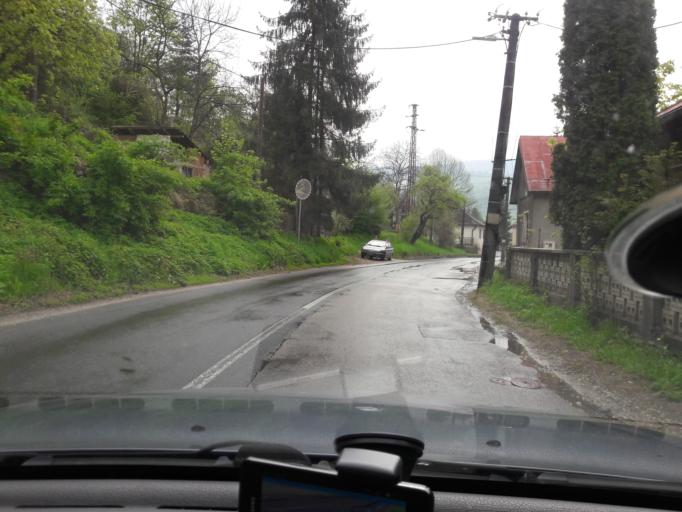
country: SK
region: Banskobystricky
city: Tisovec
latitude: 48.6883
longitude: 19.9337
